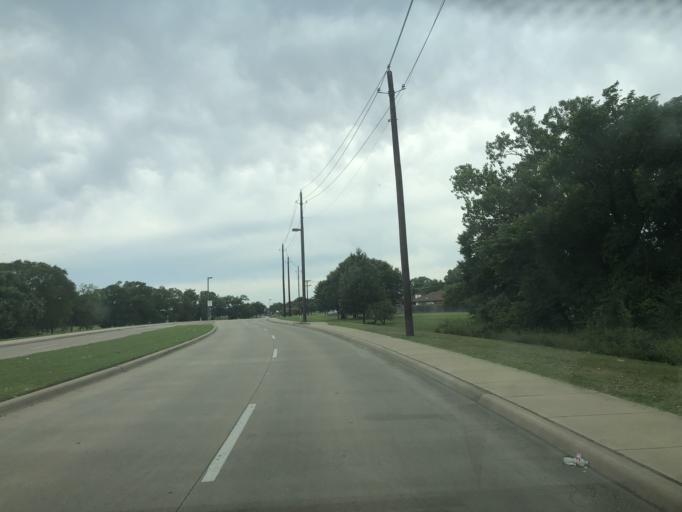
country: US
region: Texas
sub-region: Dallas County
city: Irving
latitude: 32.7845
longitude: -96.9752
